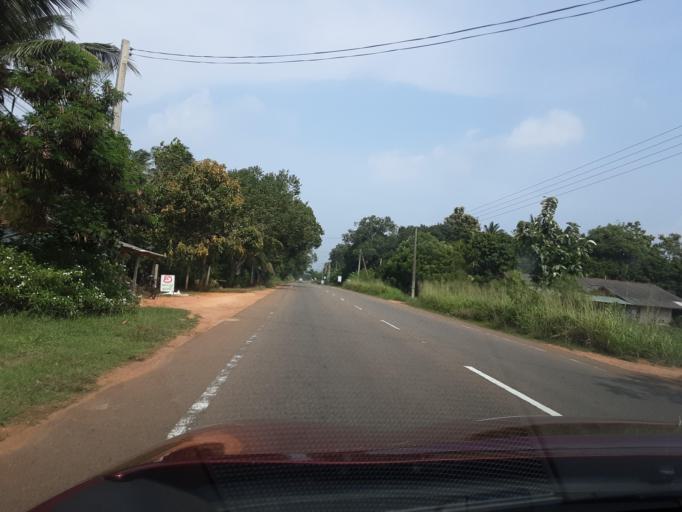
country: LK
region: North Central
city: Anuradhapura
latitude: 8.3289
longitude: 80.5010
